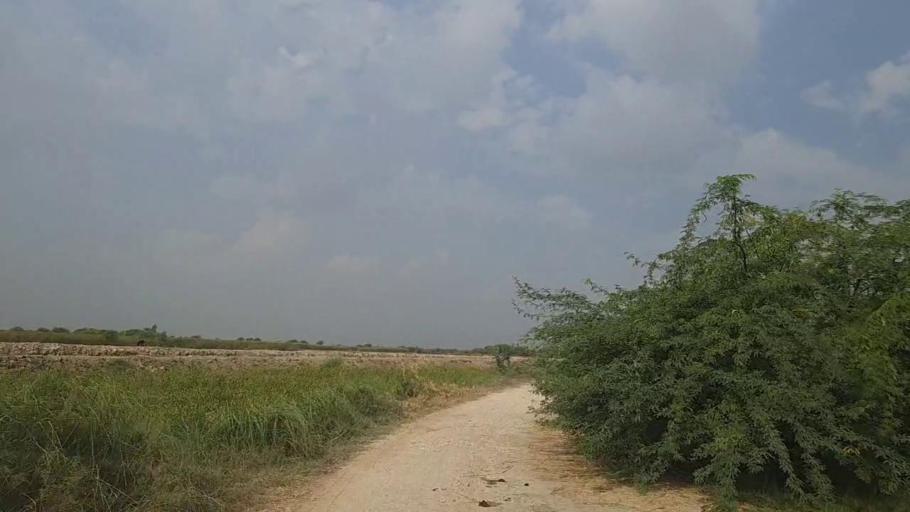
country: PK
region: Sindh
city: Daro Mehar
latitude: 24.6931
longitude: 68.1264
